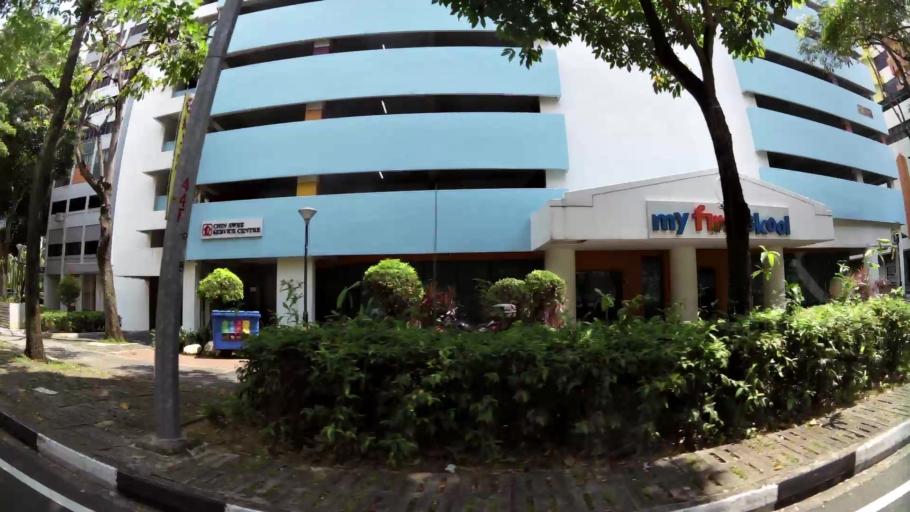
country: SG
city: Singapore
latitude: 1.2876
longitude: 103.8409
